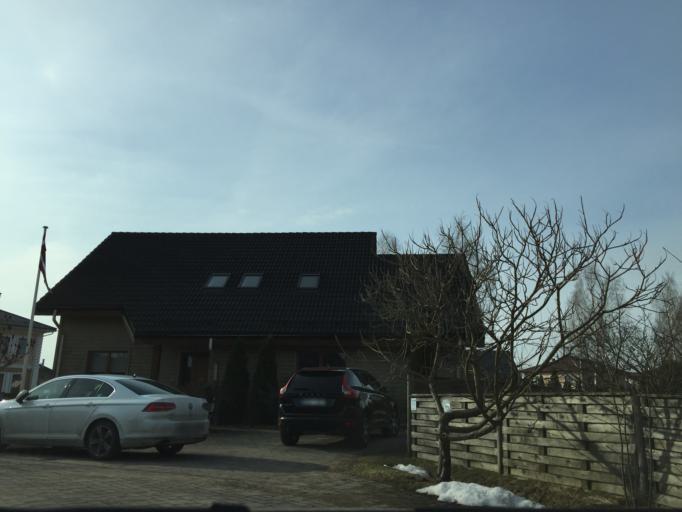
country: LV
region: Stopini
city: Ulbroka
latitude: 56.9310
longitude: 24.2592
